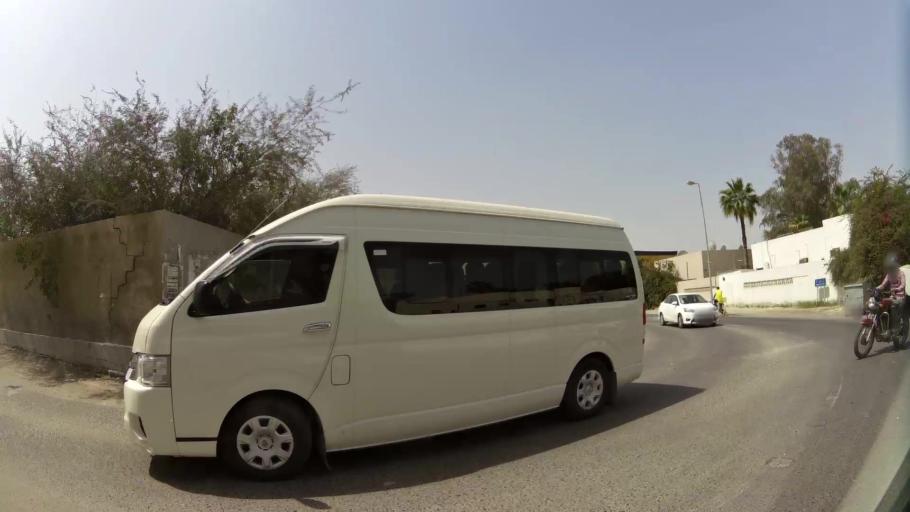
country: BH
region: Manama
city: Jidd Hafs
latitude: 26.2242
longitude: 50.4776
